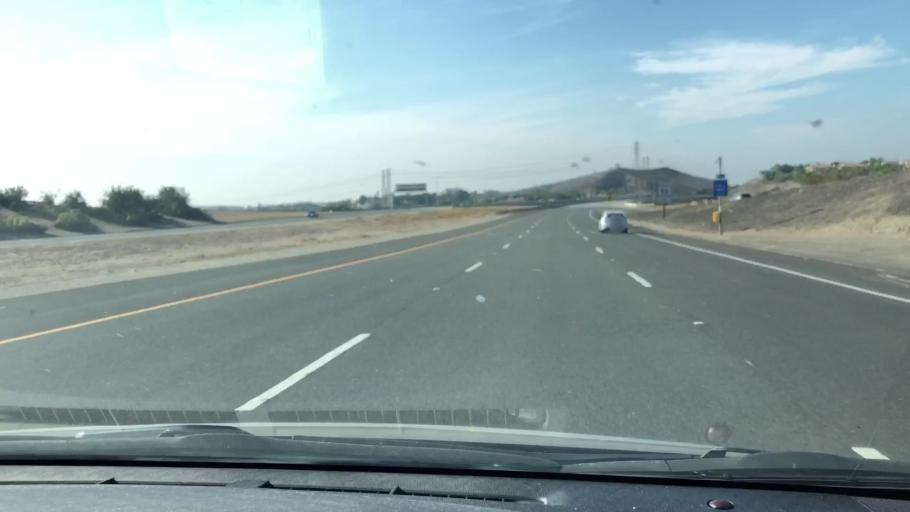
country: US
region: California
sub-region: Orange County
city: Portola Hills
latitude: 33.6558
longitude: -117.6268
